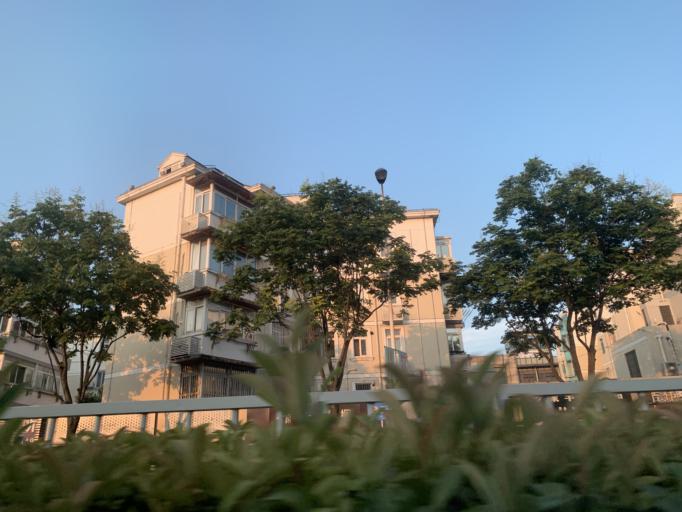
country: CN
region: Shanghai Shi
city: Huamu
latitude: 31.1857
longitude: 121.5502
